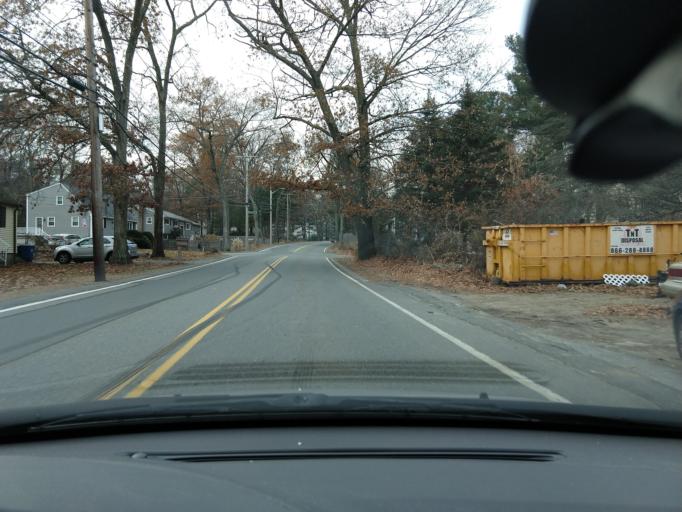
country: US
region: Massachusetts
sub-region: Middlesex County
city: Billerica
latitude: 42.5578
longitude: -71.2865
